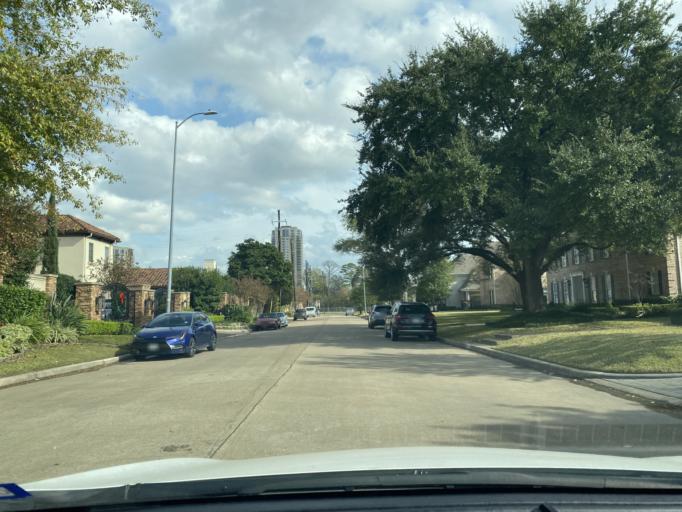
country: US
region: Texas
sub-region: Harris County
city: Hunters Creek Village
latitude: 29.7557
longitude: -95.4651
